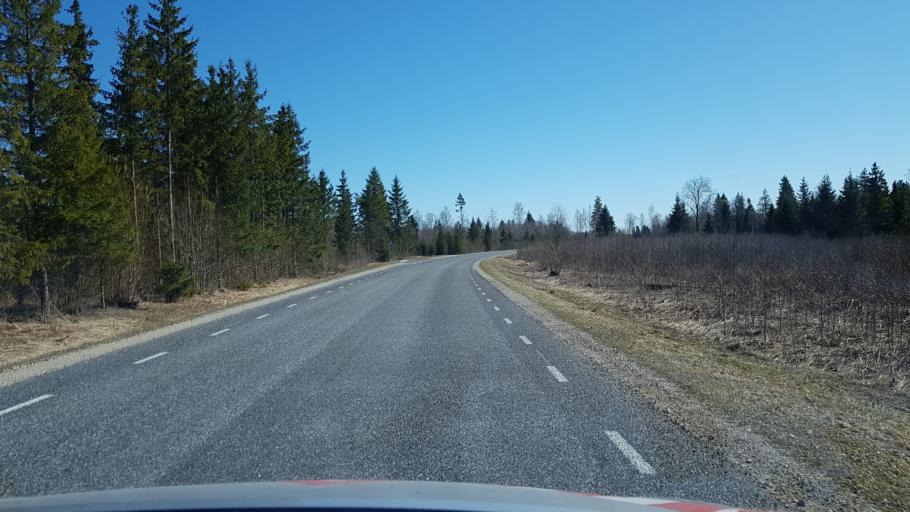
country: EE
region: Laeaene-Virumaa
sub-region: Someru vald
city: Someru
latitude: 59.3898
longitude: 26.4397
